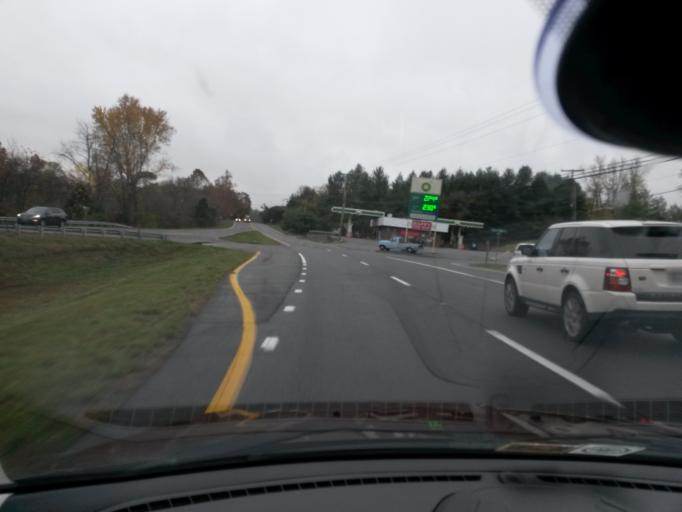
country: US
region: Virginia
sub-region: Botetourt County
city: Fincastle
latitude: 37.4916
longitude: -79.8772
